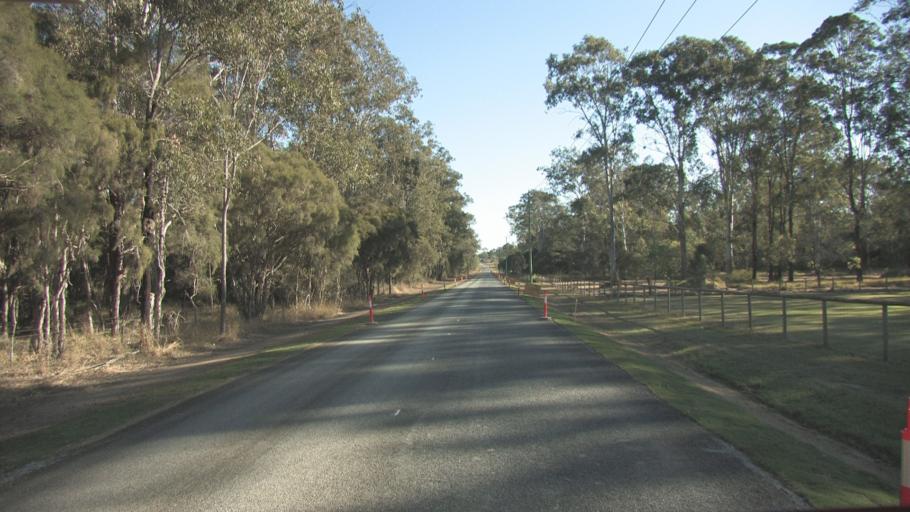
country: AU
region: Queensland
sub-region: Logan
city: Cedar Vale
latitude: -27.8335
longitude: 153.0005
